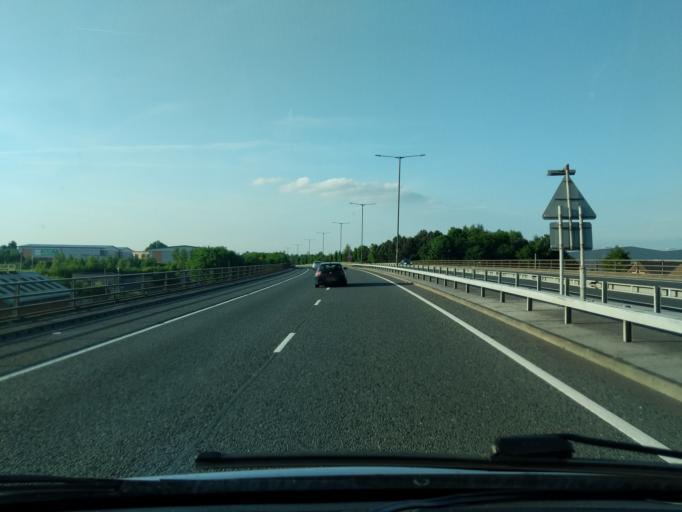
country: GB
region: England
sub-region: St. Helens
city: St Helens
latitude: 53.4226
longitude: -2.7413
